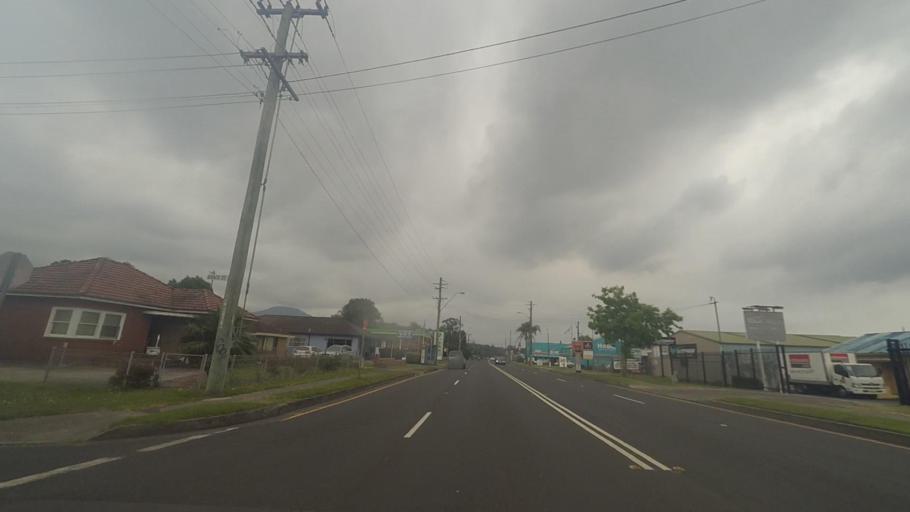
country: AU
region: New South Wales
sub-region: Wollongong
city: Cordeaux Heights
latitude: -34.4526
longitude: 150.8468
